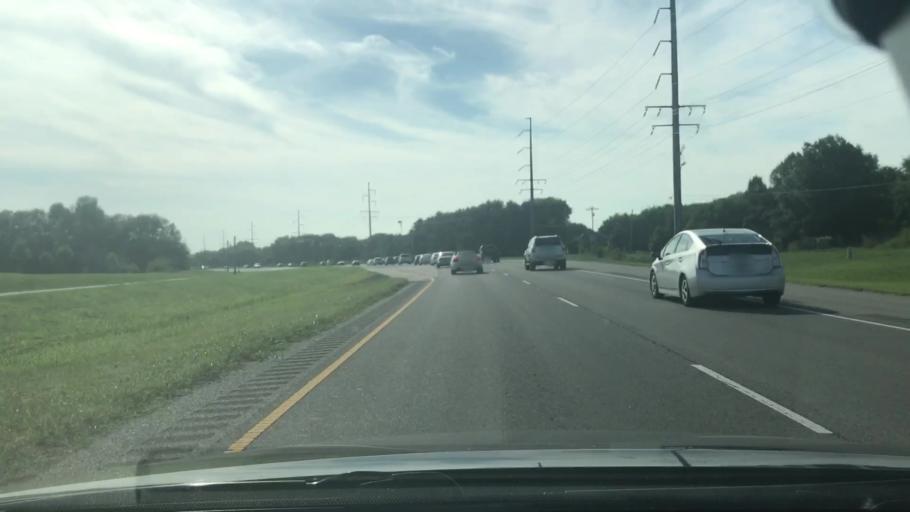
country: US
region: Tennessee
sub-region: Williamson County
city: Franklin
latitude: 35.9481
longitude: -86.8609
